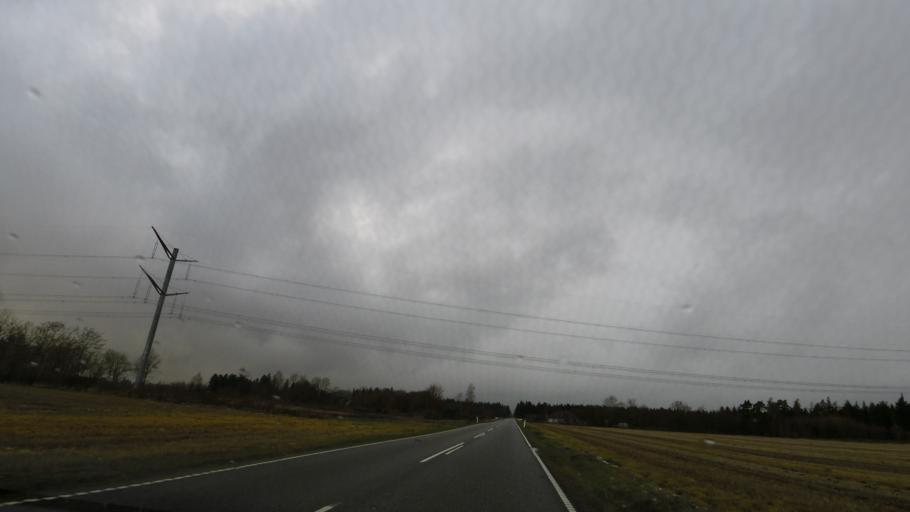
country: DK
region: Central Jutland
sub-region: Ikast-Brande Kommune
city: Brande
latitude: 55.9901
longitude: 9.2137
